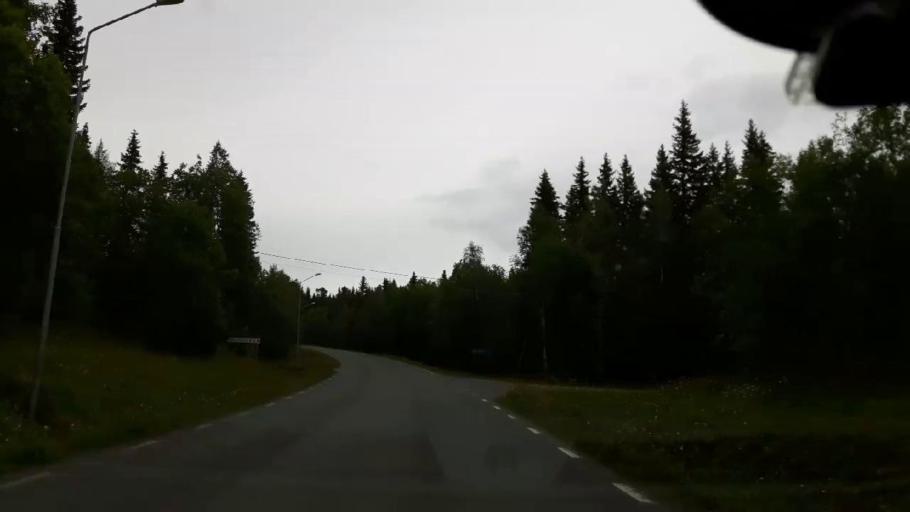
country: SE
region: Jaemtland
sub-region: Krokoms Kommun
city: Valla
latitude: 63.6477
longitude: 13.8305
